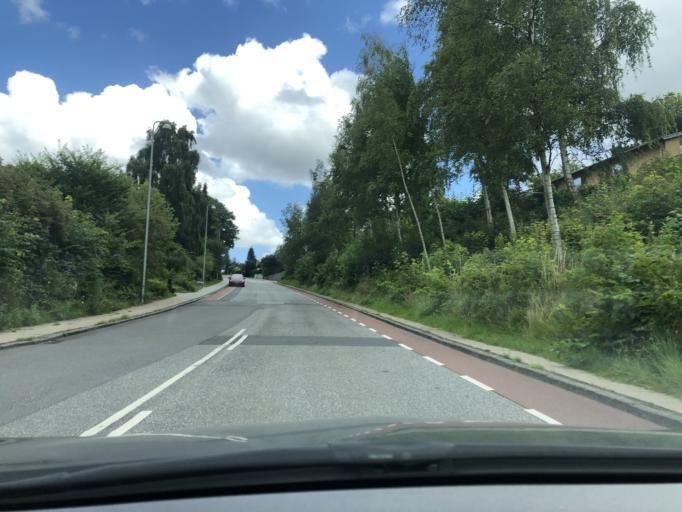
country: DK
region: South Denmark
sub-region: Vejle Kommune
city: Vejle
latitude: 55.6982
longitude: 9.5002
